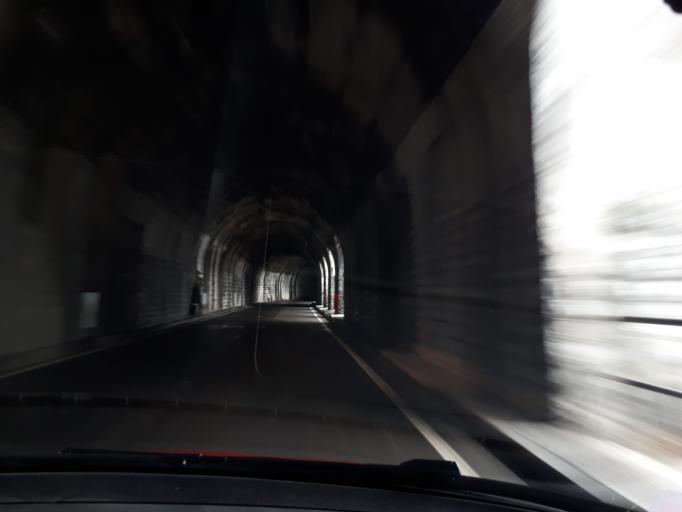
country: IT
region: Lombardy
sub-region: Provincia di Lecco
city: Varenna
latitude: 46.0236
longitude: 9.2852
